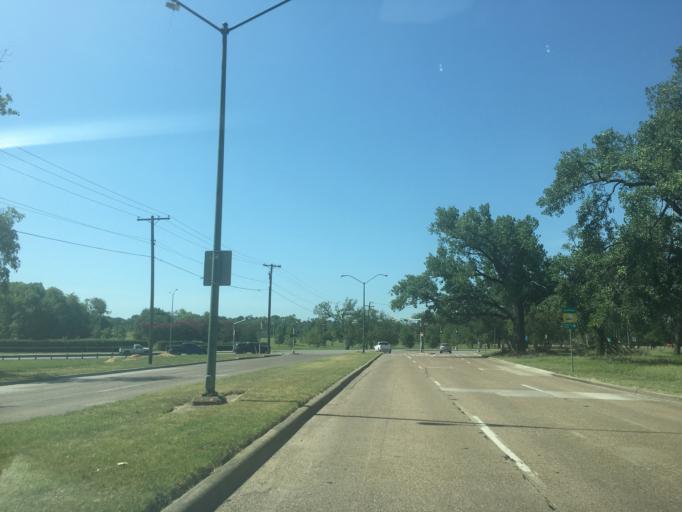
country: US
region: Texas
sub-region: Dallas County
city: Highland Park
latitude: 32.8630
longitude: -96.7180
